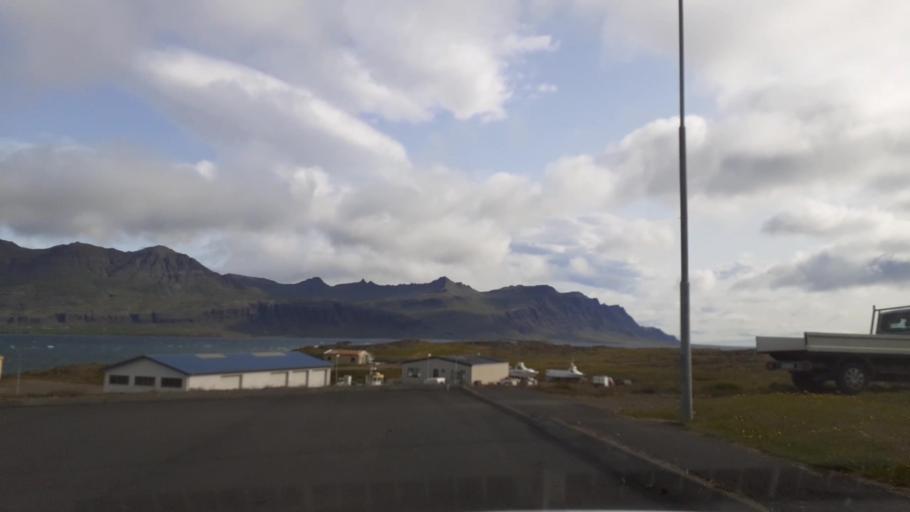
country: IS
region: East
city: Reydarfjoerdur
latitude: 64.6569
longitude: -14.2776
